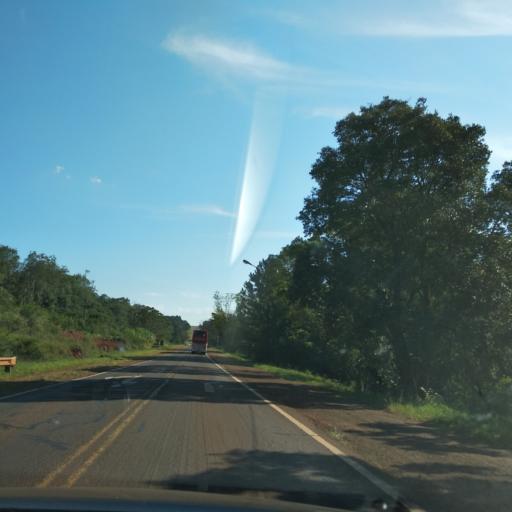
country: AR
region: Misiones
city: Santo Pipo
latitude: -27.1521
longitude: -55.4193
